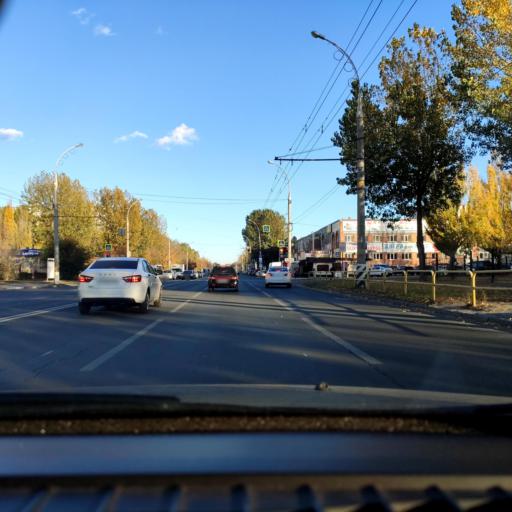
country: RU
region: Samara
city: Tol'yatti
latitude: 53.5078
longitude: 49.2632
